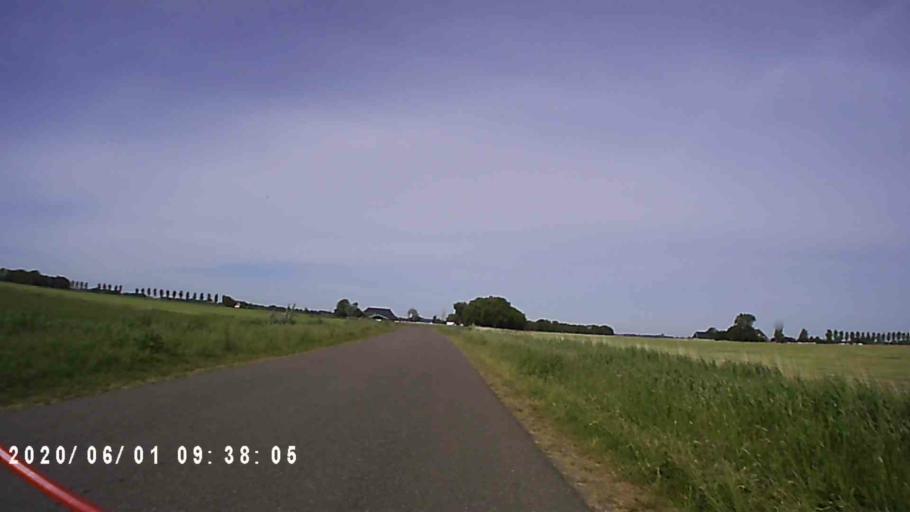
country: NL
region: Friesland
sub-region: Gemeente Het Bildt
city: Sint Annaparochie
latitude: 53.2572
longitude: 5.6872
